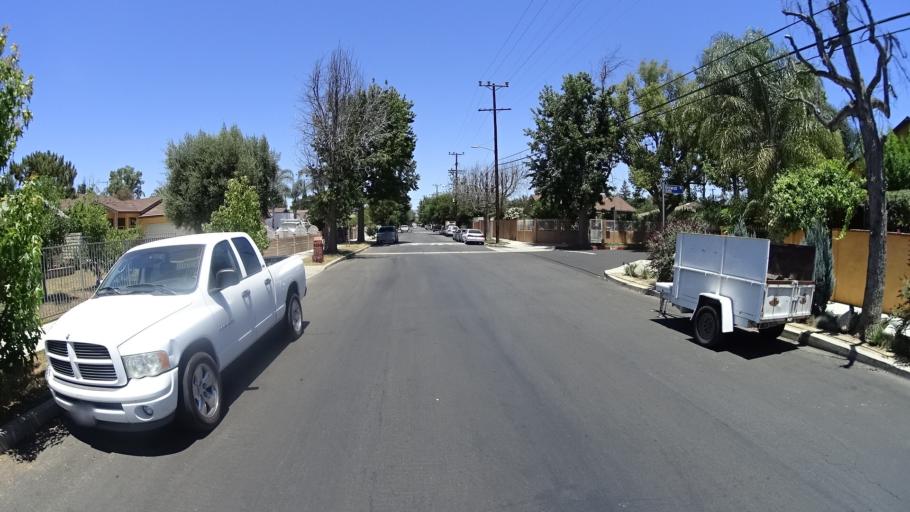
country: US
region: California
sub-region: Los Angeles County
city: Van Nuys
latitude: 34.2101
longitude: -118.4706
